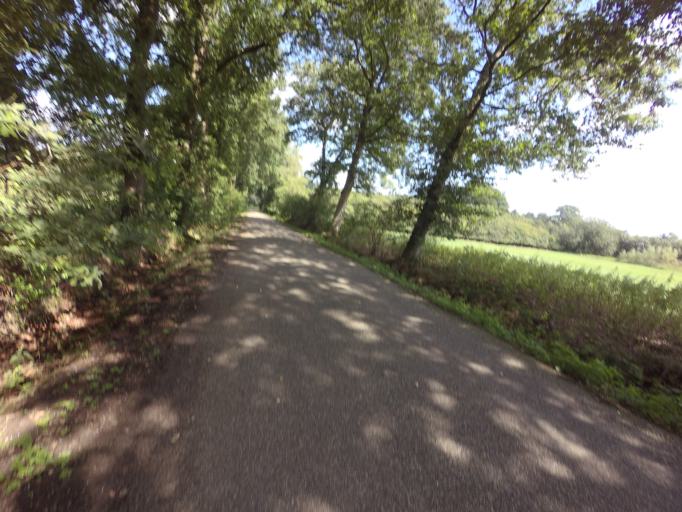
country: NL
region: Gelderland
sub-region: Gemeente Ede
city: Otterlo
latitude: 52.0515
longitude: 5.7316
